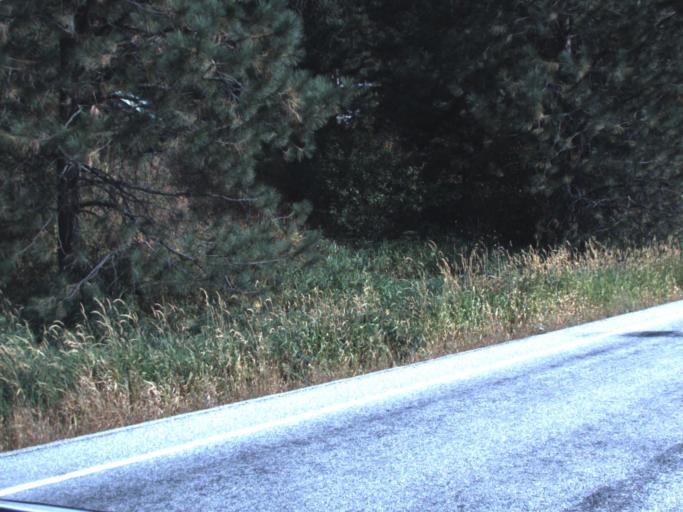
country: US
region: Washington
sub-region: Pend Oreille County
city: Newport
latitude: 48.1319
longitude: -117.2802
